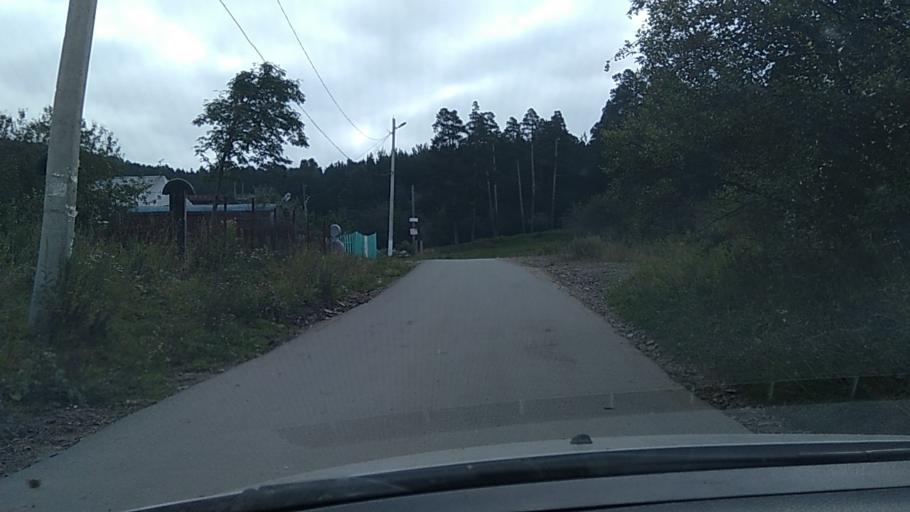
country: RU
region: Chelyabinsk
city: Zlatoust
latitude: 55.1709
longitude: 59.7082
